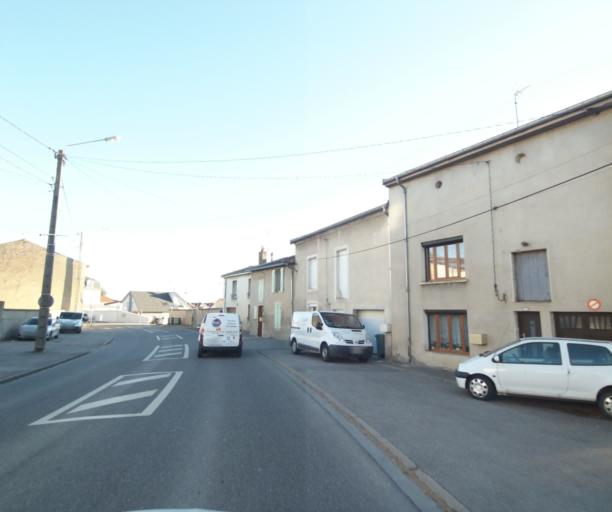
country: FR
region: Lorraine
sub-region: Departement de Meurthe-et-Moselle
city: Art-sur-Meurthe
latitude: 48.6551
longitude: 6.2648
